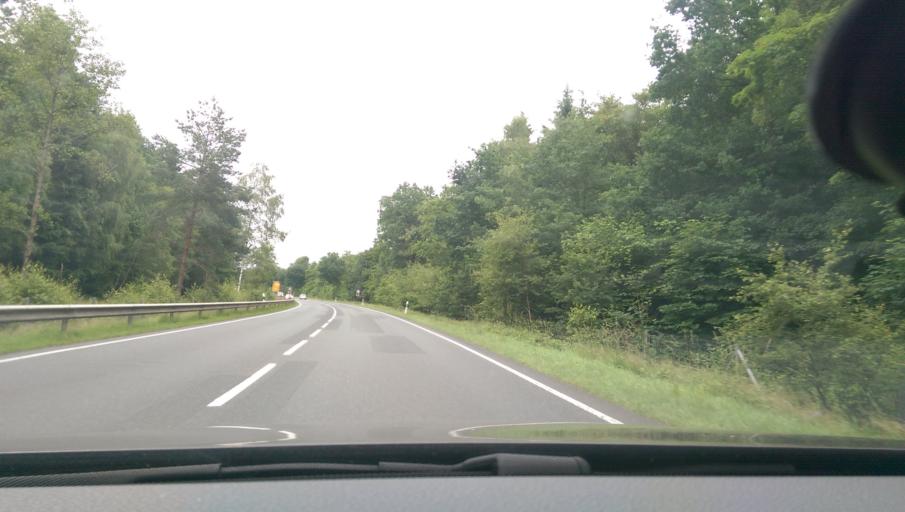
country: DE
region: Lower Saxony
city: Rotenburg
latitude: 53.1206
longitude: 9.3807
